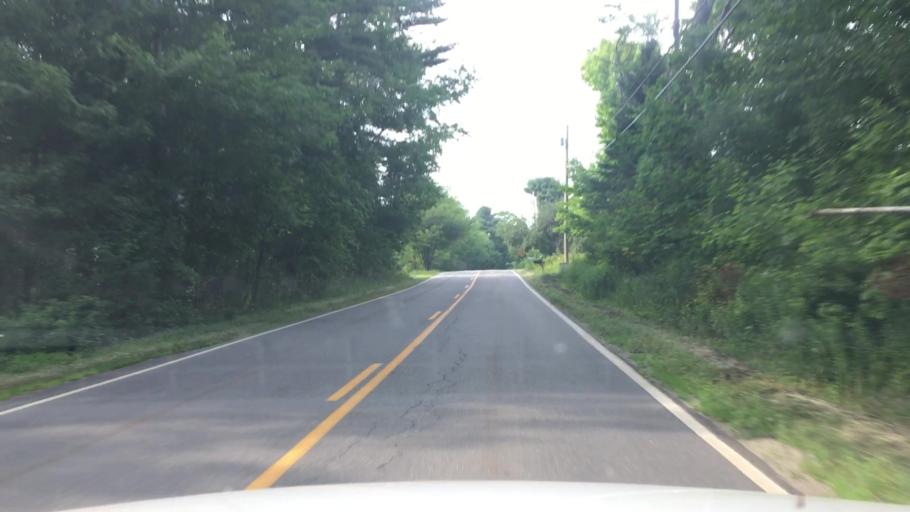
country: US
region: Maine
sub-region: Lincoln County
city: Waldoboro
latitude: 44.1594
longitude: -69.3771
